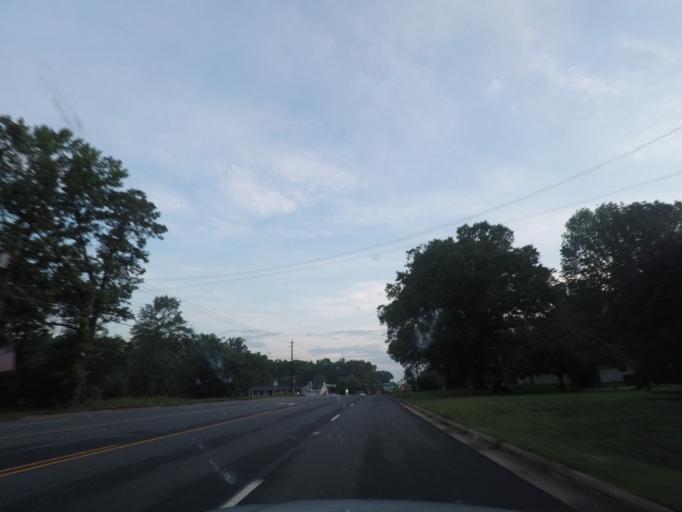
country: US
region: North Carolina
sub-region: Person County
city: Roxboro
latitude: 36.2167
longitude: -78.9253
